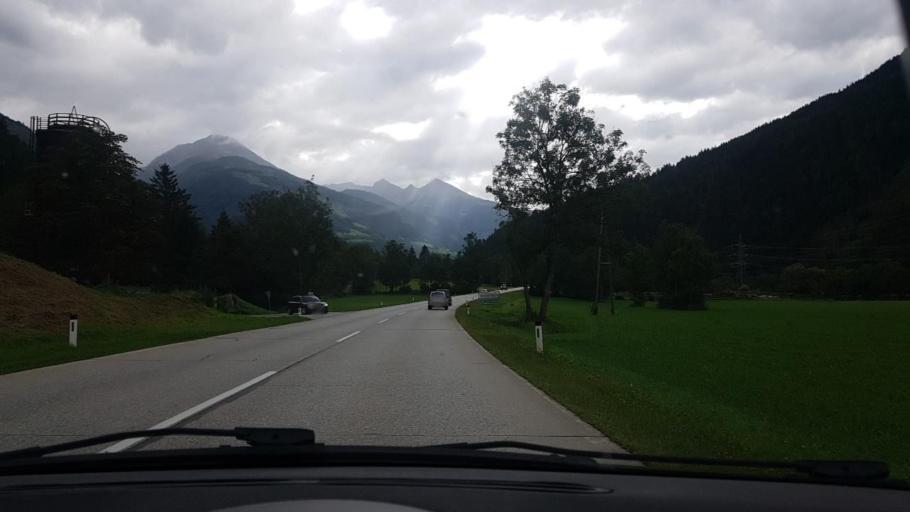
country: AT
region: Carinthia
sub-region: Politischer Bezirk Spittal an der Drau
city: Flattach
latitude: 46.9355
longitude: 13.1565
